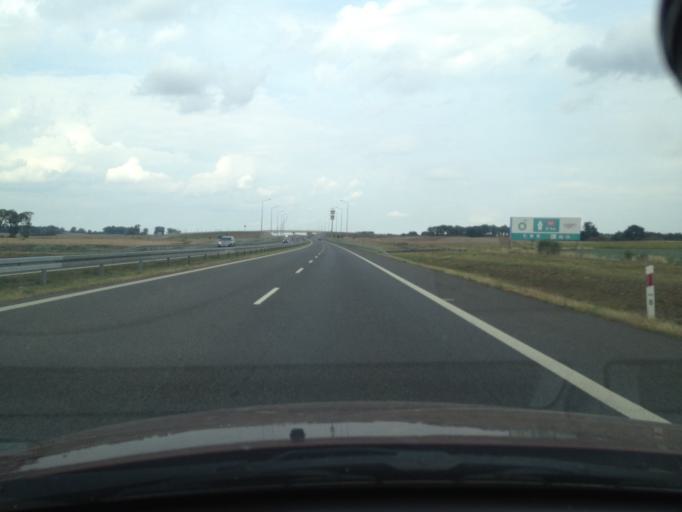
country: PL
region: West Pomeranian Voivodeship
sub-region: Powiat pyrzycki
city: Kozielice
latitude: 53.0430
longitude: 14.8660
